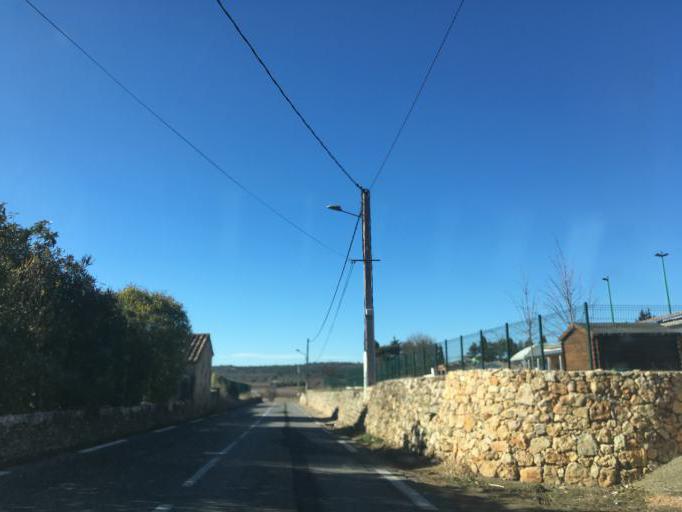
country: FR
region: Provence-Alpes-Cote d'Azur
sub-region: Departement du Var
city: Barjols
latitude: 43.5935
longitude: 6.0136
